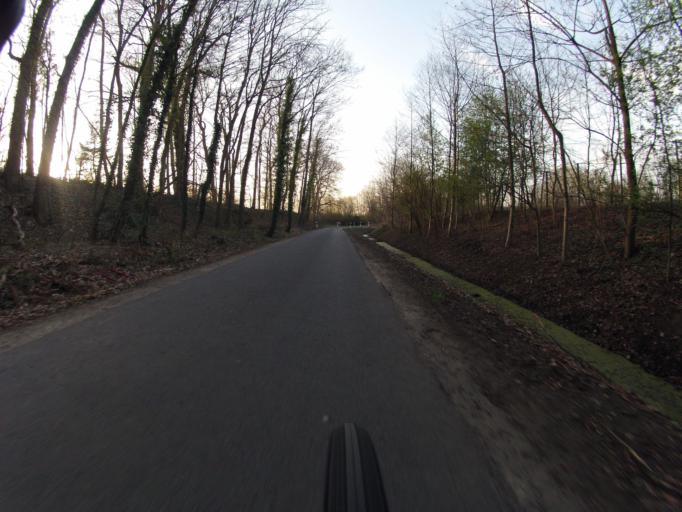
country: DE
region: North Rhine-Westphalia
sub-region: Regierungsbezirk Munster
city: Birgte
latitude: 52.2402
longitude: 7.6739
